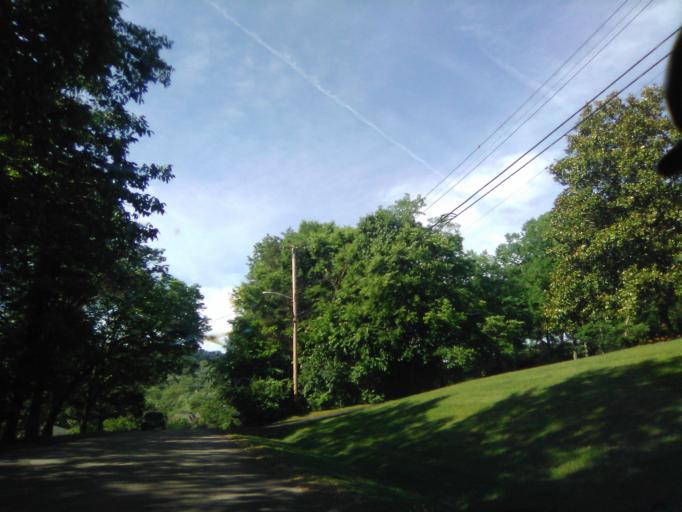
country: US
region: Tennessee
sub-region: Davidson County
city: Belle Meade
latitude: 36.1199
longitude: -86.9058
